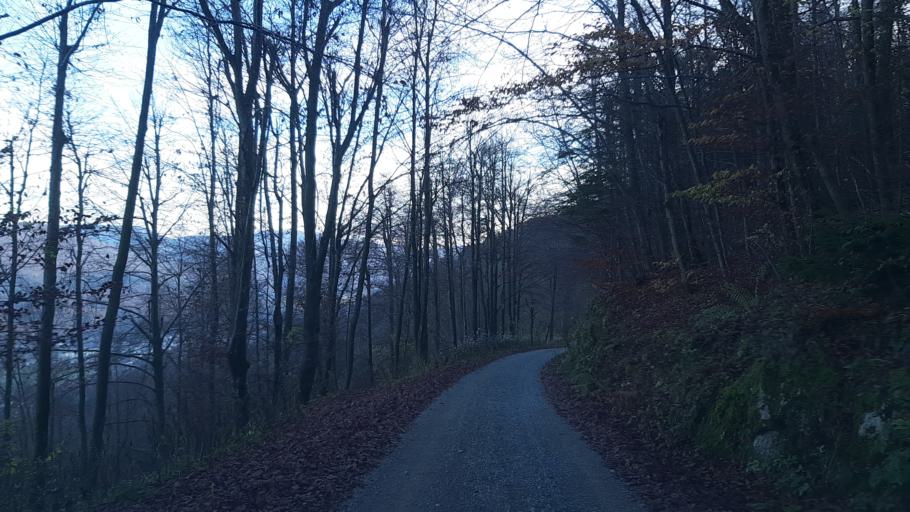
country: SI
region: Borovnica
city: Borovnica
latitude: 45.9306
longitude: 14.3373
